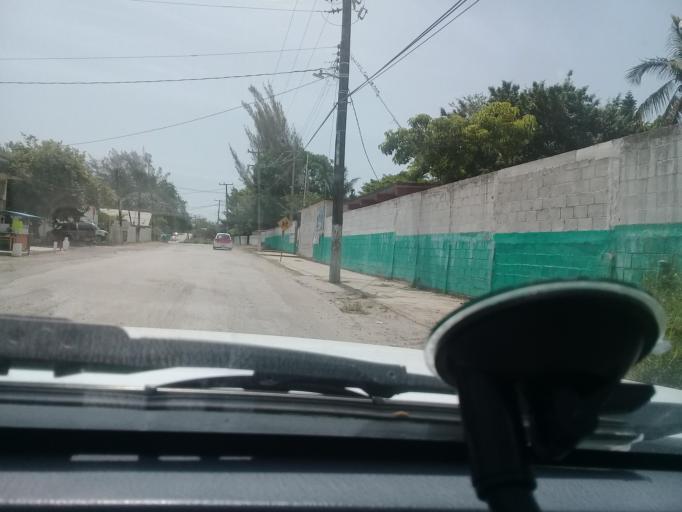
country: MX
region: Veracruz
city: Anahuac
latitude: 22.2289
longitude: -97.8274
